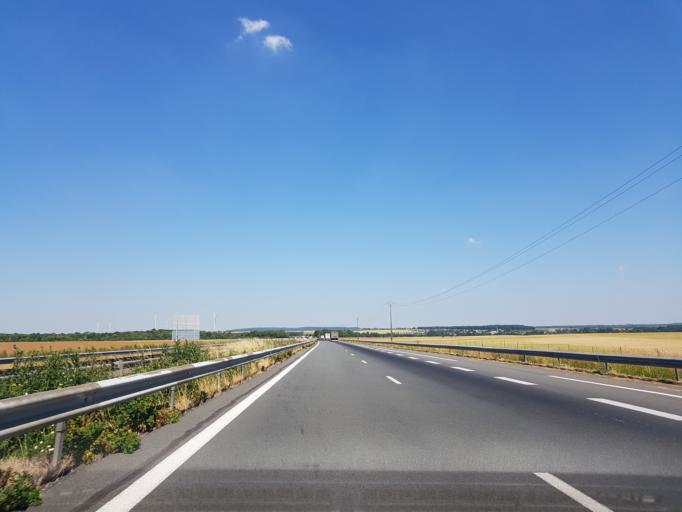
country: FR
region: Nord-Pas-de-Calais
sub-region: Departement du Nord
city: Marcoing
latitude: 50.0973
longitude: 3.1686
